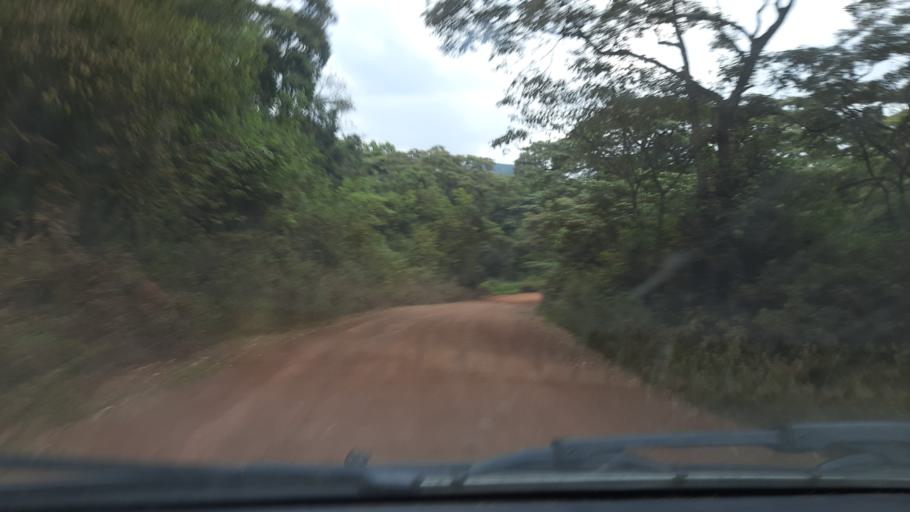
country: TZ
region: Kilimanjaro
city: Moshi
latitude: -2.8602
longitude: 37.2535
